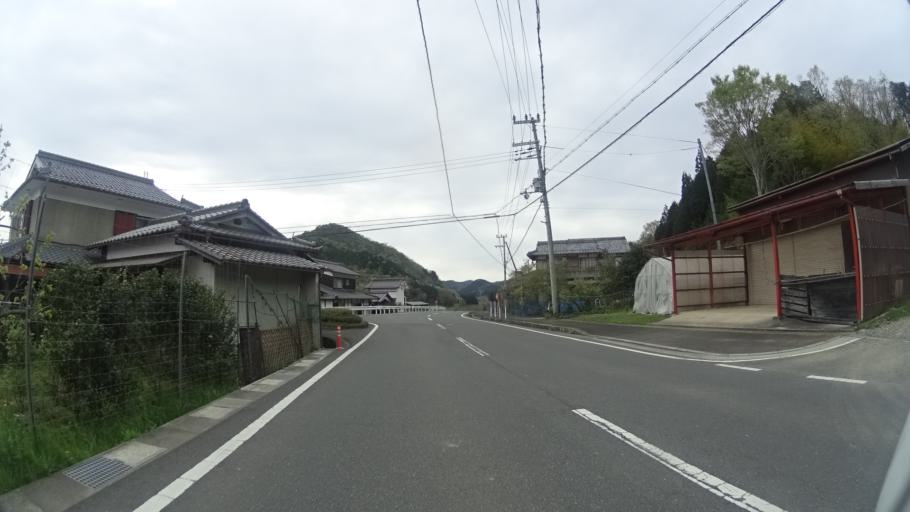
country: JP
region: Kyoto
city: Ayabe
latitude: 35.1801
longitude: 135.4378
